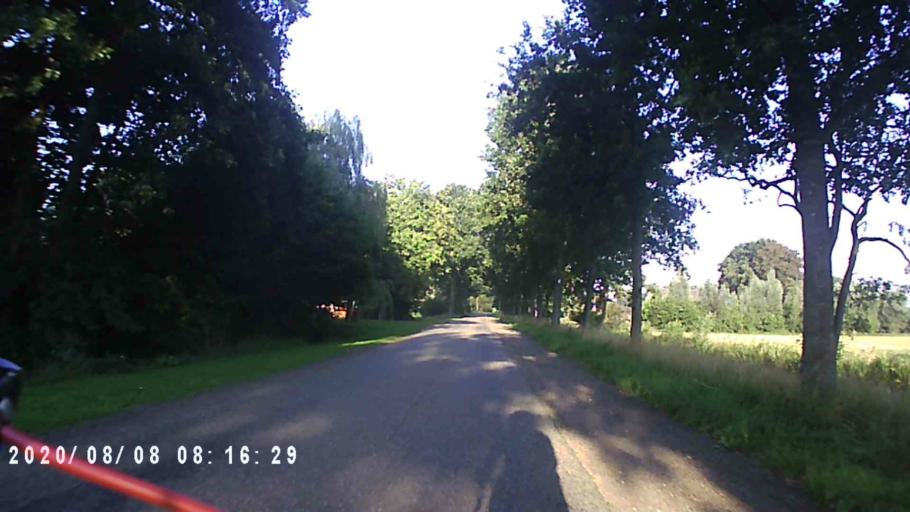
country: NL
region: Groningen
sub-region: Gemeente Leek
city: Leek
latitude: 53.0956
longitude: 6.3358
